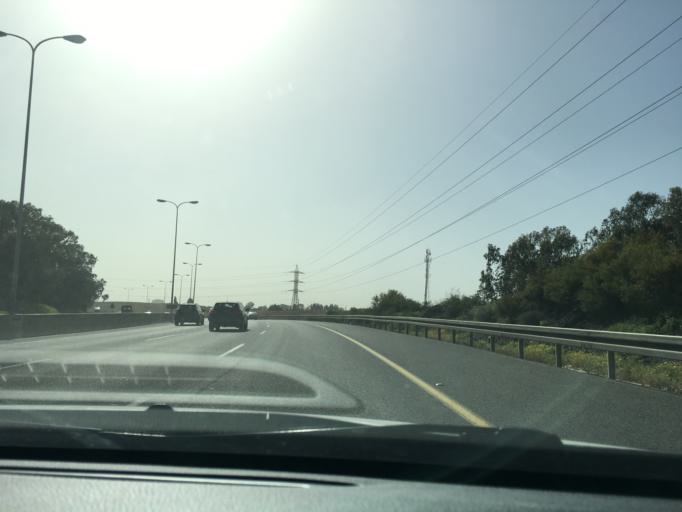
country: IL
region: Central District
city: Hod HaSharon
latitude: 32.1573
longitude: 34.8739
